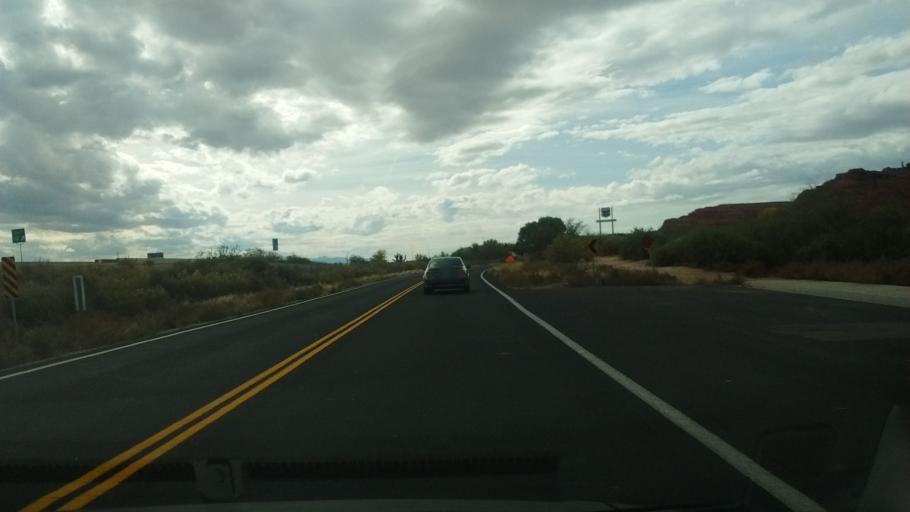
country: US
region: Utah
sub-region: Washington County
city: Washington
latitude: 37.1315
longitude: -113.5221
